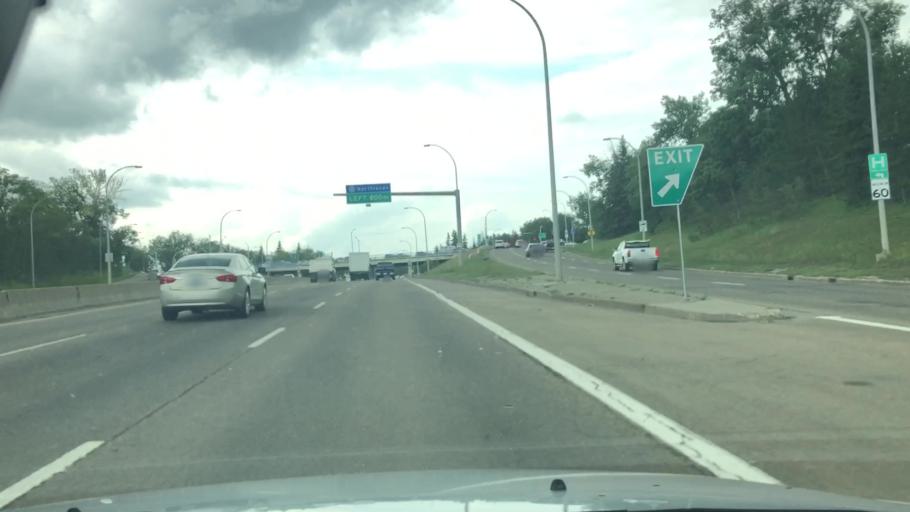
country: CA
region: Alberta
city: Edmonton
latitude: 53.5611
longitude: -113.4439
